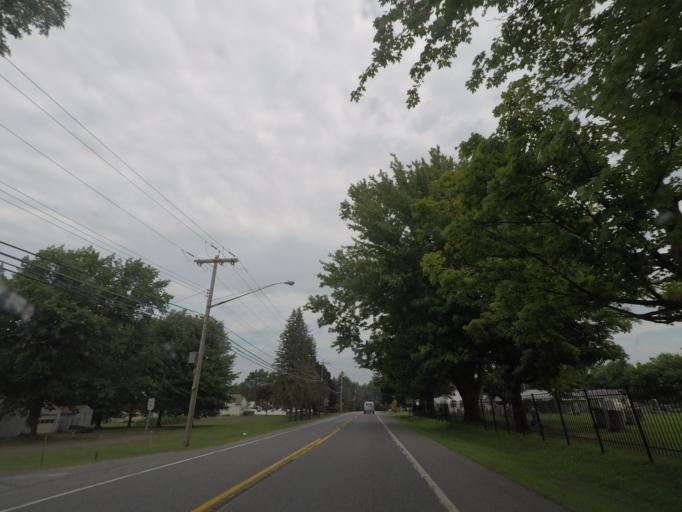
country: US
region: New York
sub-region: Saratoga County
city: Waterford
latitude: 42.8041
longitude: -73.6836
